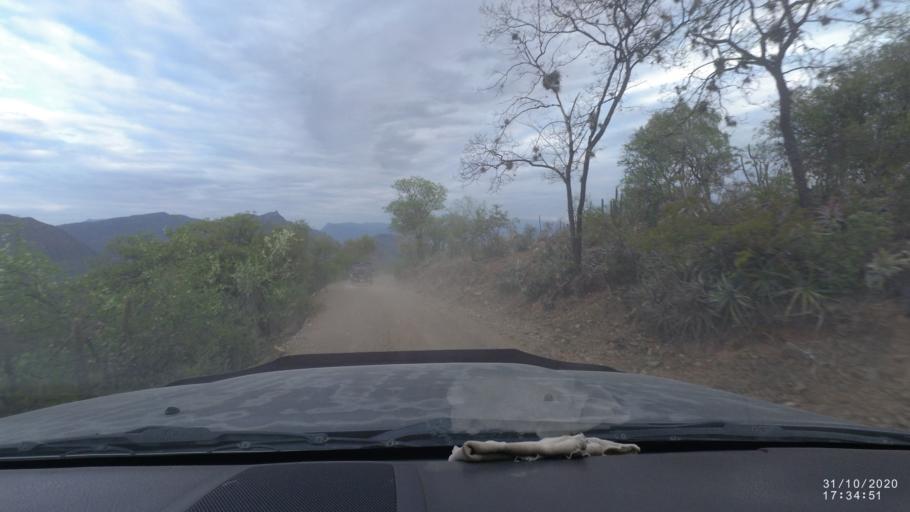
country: BO
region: Chuquisaca
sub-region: Provincia Zudanez
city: Mojocoya
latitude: -18.6020
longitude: -64.5484
